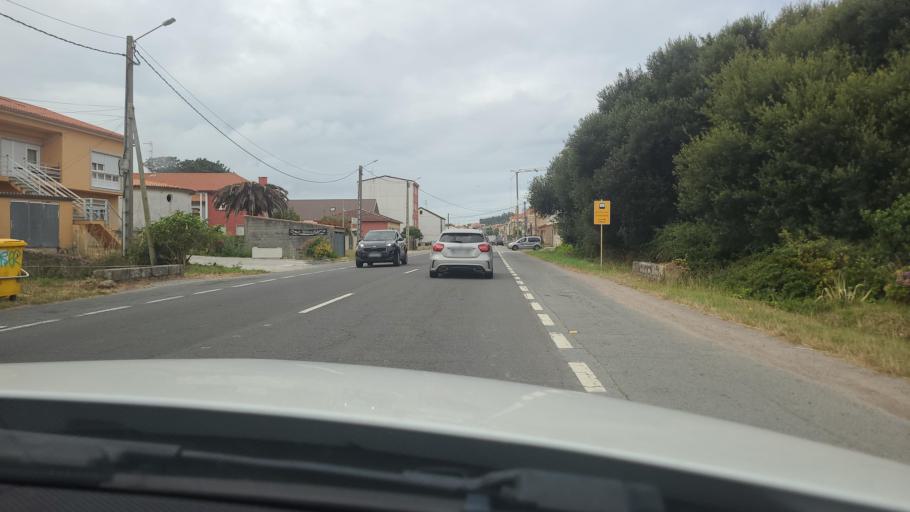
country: ES
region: Galicia
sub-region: Provincia da Coruna
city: Fisterra
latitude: 42.9263
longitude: -9.2598
